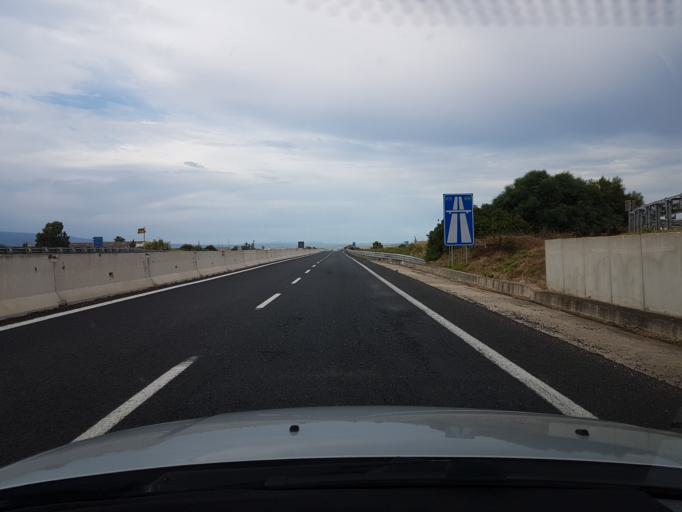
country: IT
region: Sardinia
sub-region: Provincia di Oristano
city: Siamaggiore
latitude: 39.9639
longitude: 8.6197
